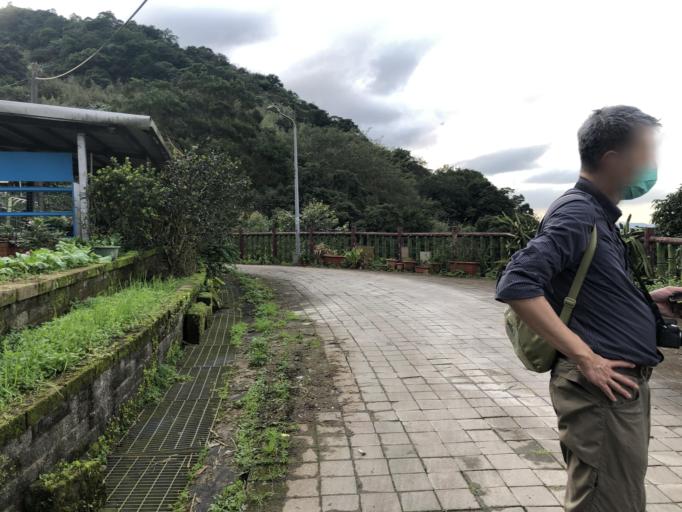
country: TW
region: Taipei
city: Taipei
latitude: 25.0248
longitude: 121.6596
